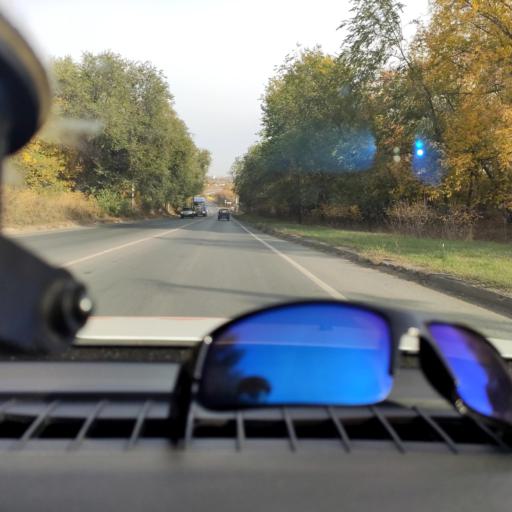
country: RU
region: Samara
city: Novokuybyshevsk
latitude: 53.0892
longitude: 50.0650
